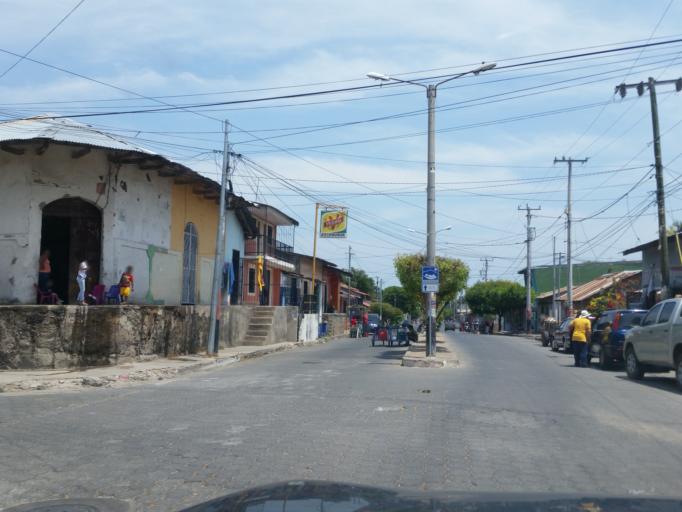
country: NI
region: Granada
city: Granada
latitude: 11.9284
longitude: -85.9474
